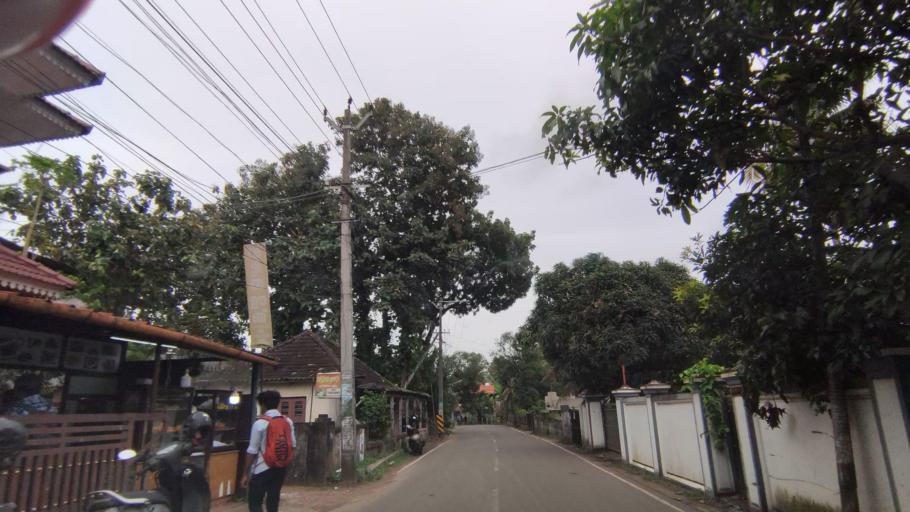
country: IN
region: Kerala
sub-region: Kottayam
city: Kottayam
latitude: 9.6520
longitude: 76.5222
